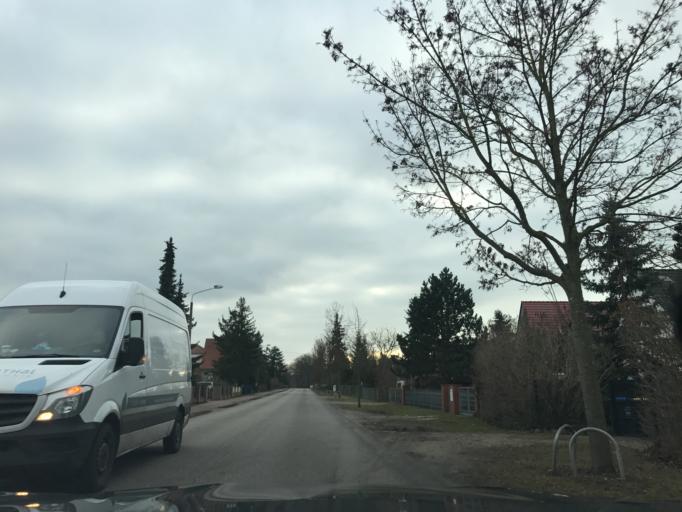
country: DE
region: Brandenburg
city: Brandenburg an der Havel
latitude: 52.3769
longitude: 12.5456
